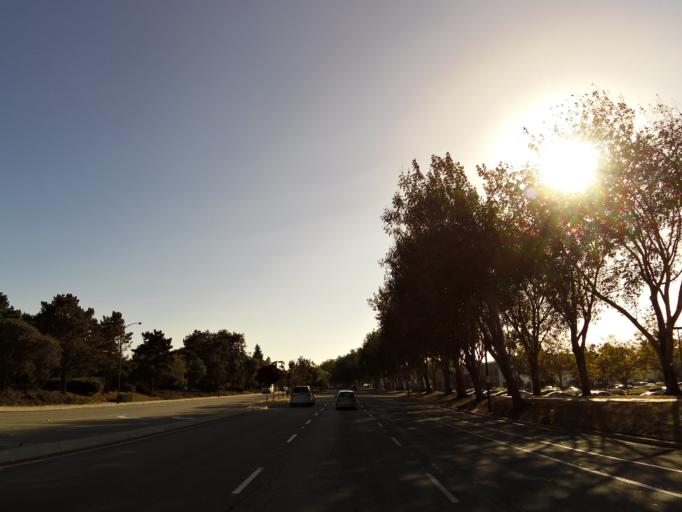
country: US
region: California
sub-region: Santa Clara County
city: Santa Clara
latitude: 37.3841
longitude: -121.9322
